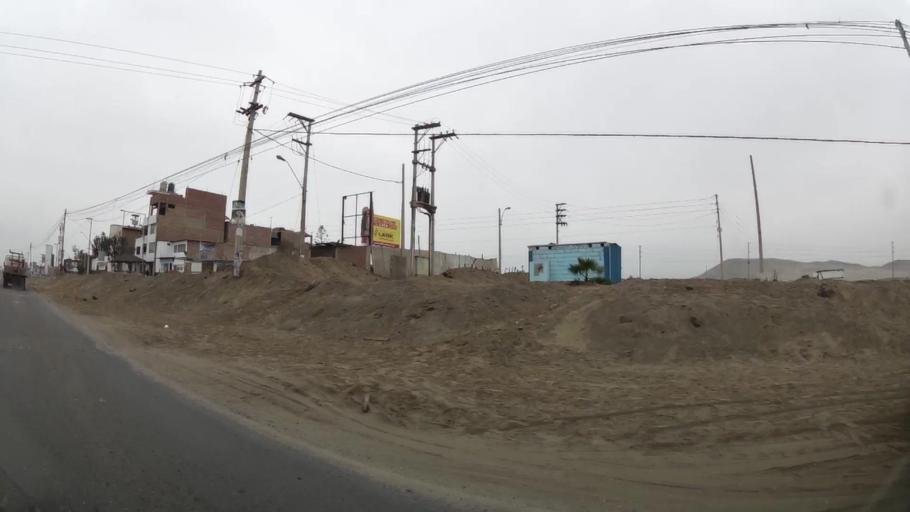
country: PE
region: Lima
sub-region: Lima
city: Punta Hermosa
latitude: -12.3248
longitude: -76.8267
